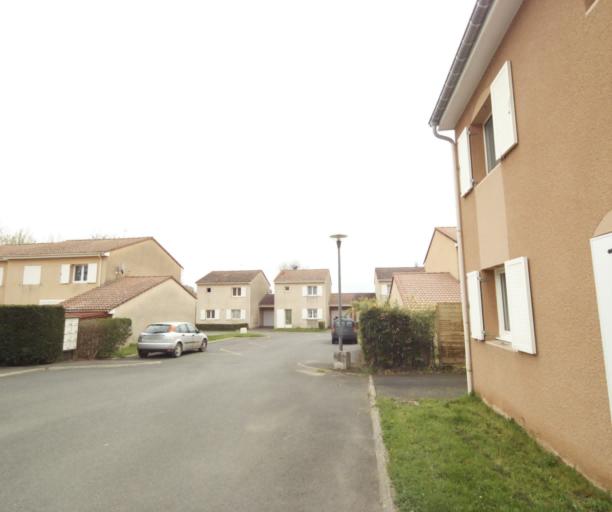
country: FR
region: Bourgogne
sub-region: Departement de Saone-et-Loire
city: Charnay-les-Macon
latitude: 46.3057
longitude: 4.7888
